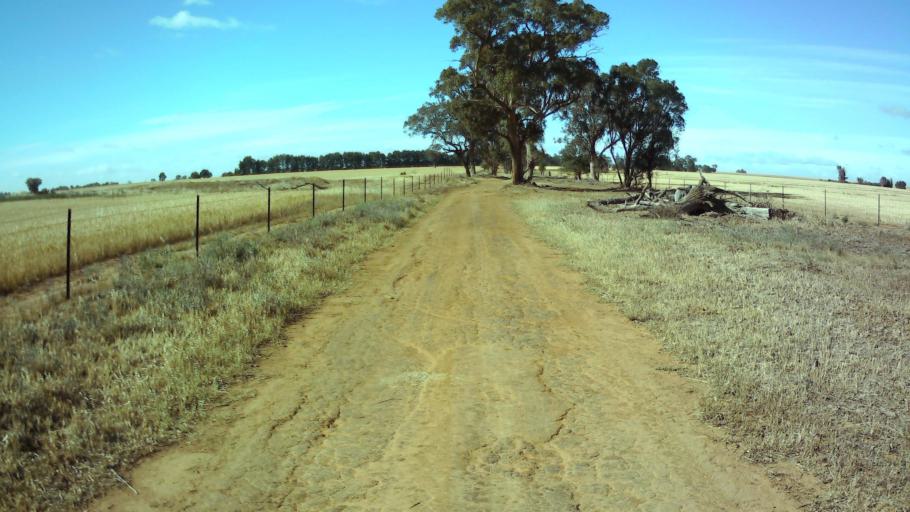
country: AU
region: New South Wales
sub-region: Weddin
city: Grenfell
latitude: -34.0547
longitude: 148.2683
